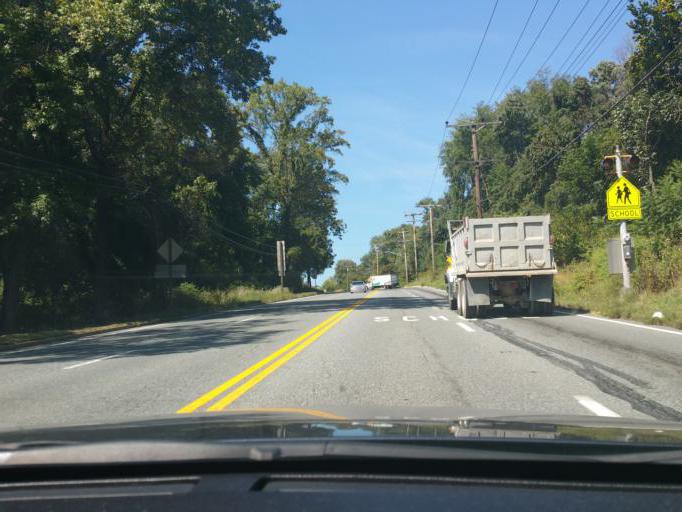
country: US
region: Maryland
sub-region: Harford County
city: Havre de Grace
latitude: 39.5604
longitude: -76.1060
